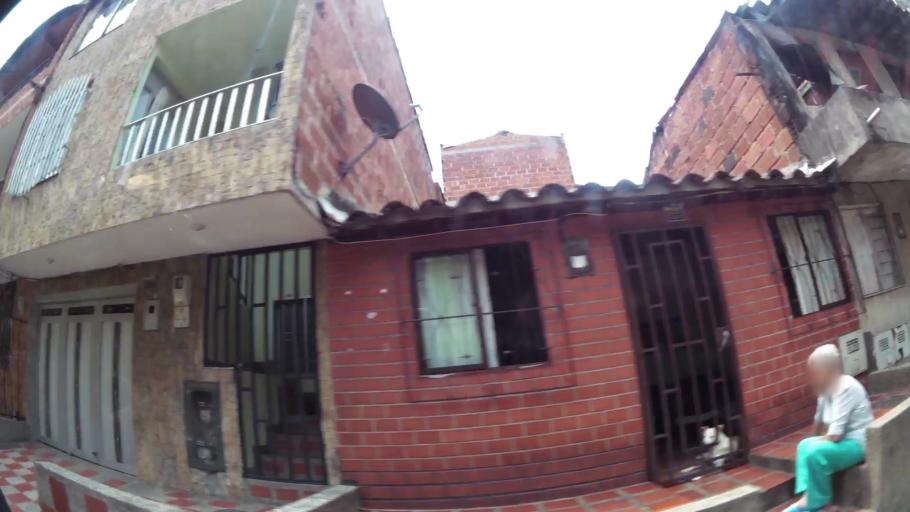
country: CO
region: Antioquia
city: Itagui
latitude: 6.1821
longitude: -75.6069
